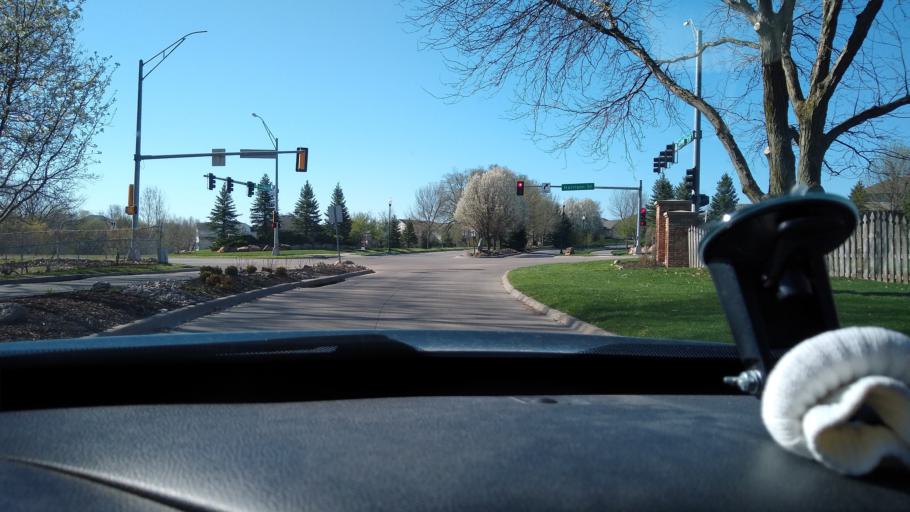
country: US
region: Nebraska
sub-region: Douglas County
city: Ralston
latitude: 41.1913
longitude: -96.0719
